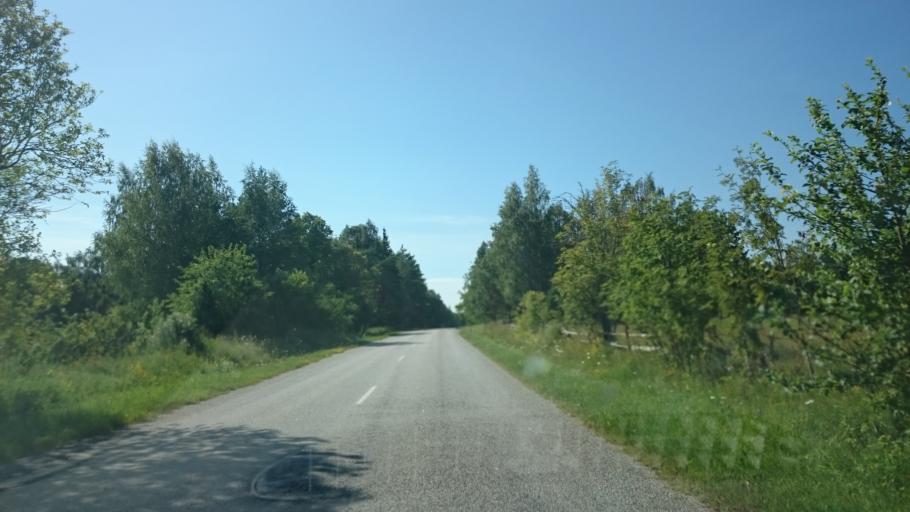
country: EE
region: Saare
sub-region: Orissaare vald
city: Orissaare
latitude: 58.5702
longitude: 22.7451
